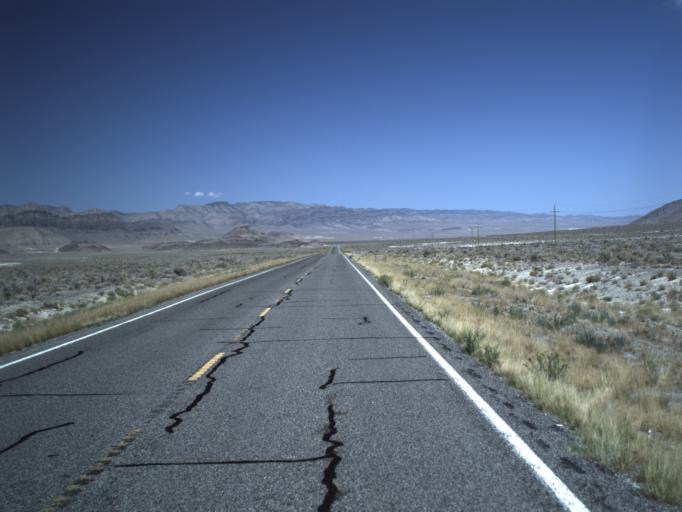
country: US
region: Utah
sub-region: Beaver County
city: Milford
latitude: 39.0329
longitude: -113.3862
